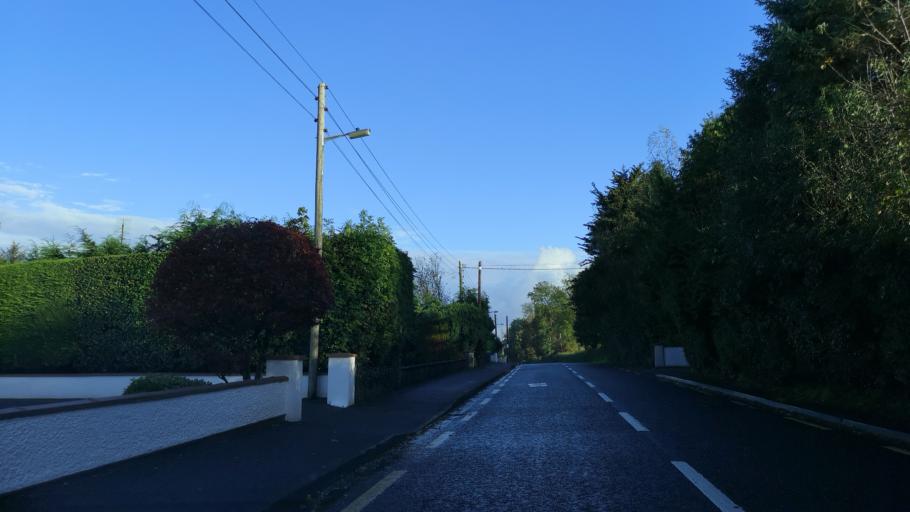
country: IE
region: Connaught
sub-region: Roscommon
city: Castlerea
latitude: 53.7630
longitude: -8.4761
